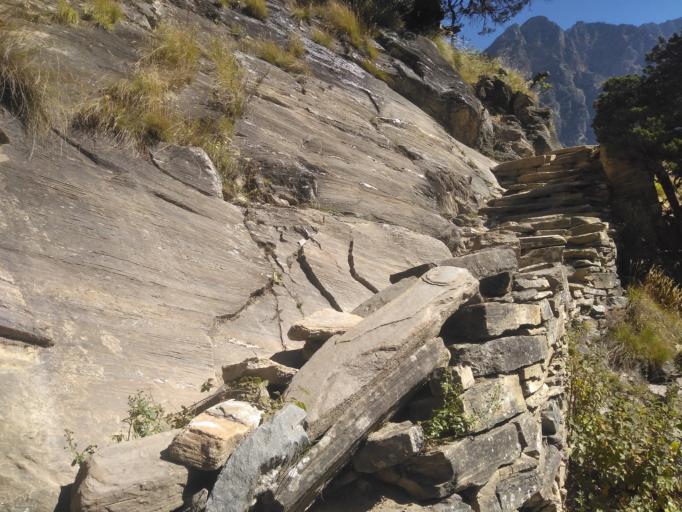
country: NP
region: Western Region
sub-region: Dhawalagiri Zone
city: Jomsom
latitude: 28.9422
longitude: 83.0597
